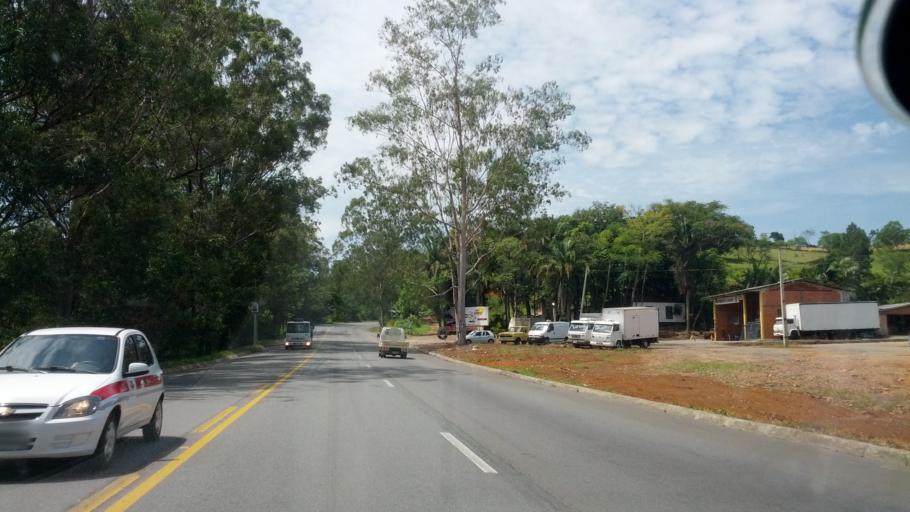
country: BR
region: Santa Catarina
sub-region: Ibirama
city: Ibirama
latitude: -27.0990
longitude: -49.5289
